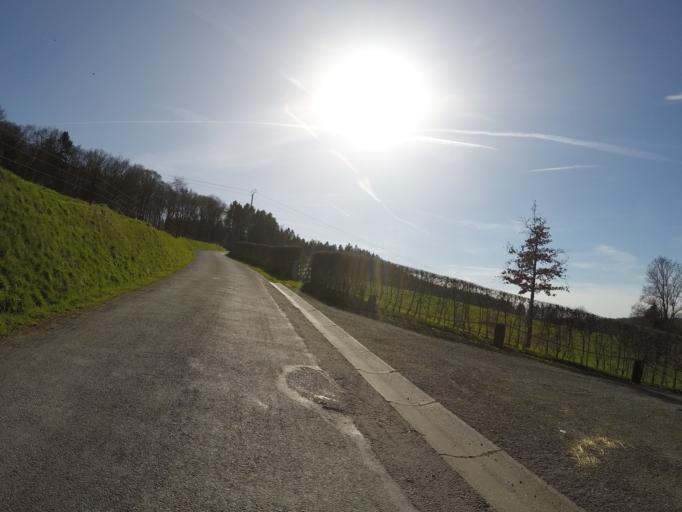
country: BE
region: Wallonia
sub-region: Province de Namur
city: Havelange
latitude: 50.4028
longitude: 5.2215
